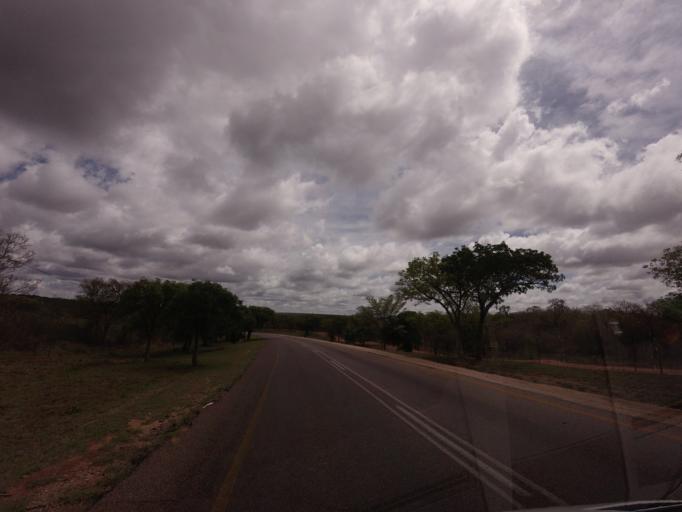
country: ZA
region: Limpopo
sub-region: Mopani District Municipality
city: Hoedspruit
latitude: -24.5483
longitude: 31.0388
